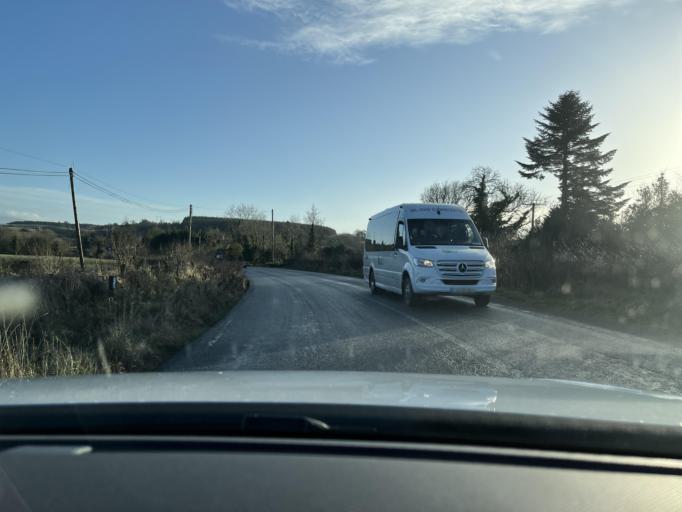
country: IE
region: Connaught
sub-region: County Leitrim
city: Manorhamilton
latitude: 54.1893
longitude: -8.1687
